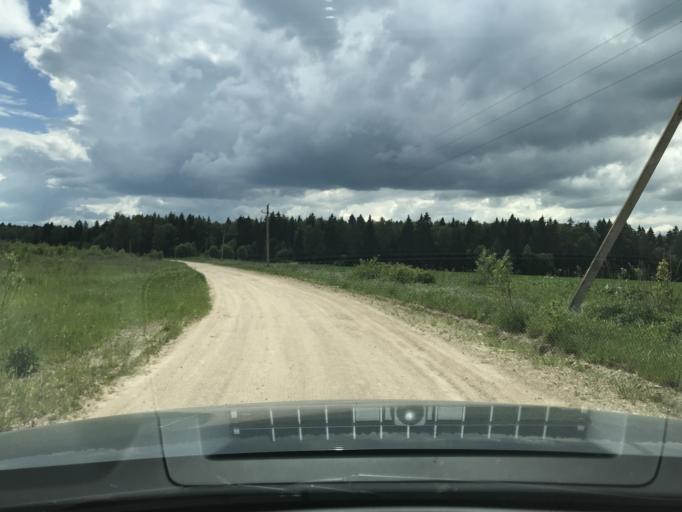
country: RU
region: Moskovskaya
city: Vereya
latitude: 55.3225
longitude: 36.3204
